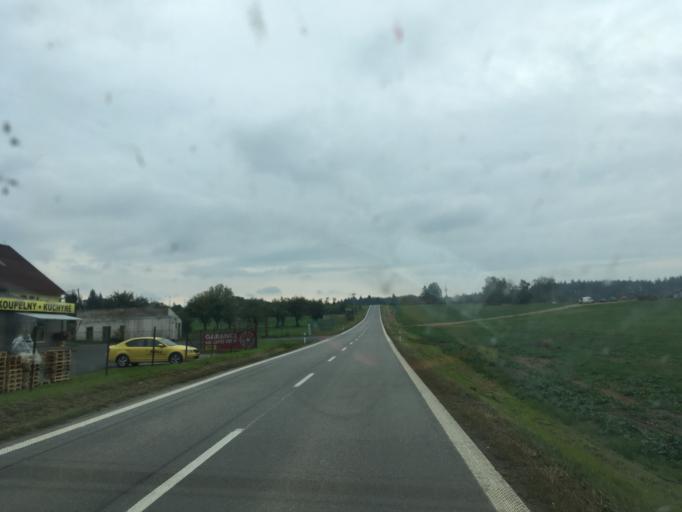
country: CZ
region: Vysocina
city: Namest' nad Oslavou
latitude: 49.1967
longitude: 16.2095
